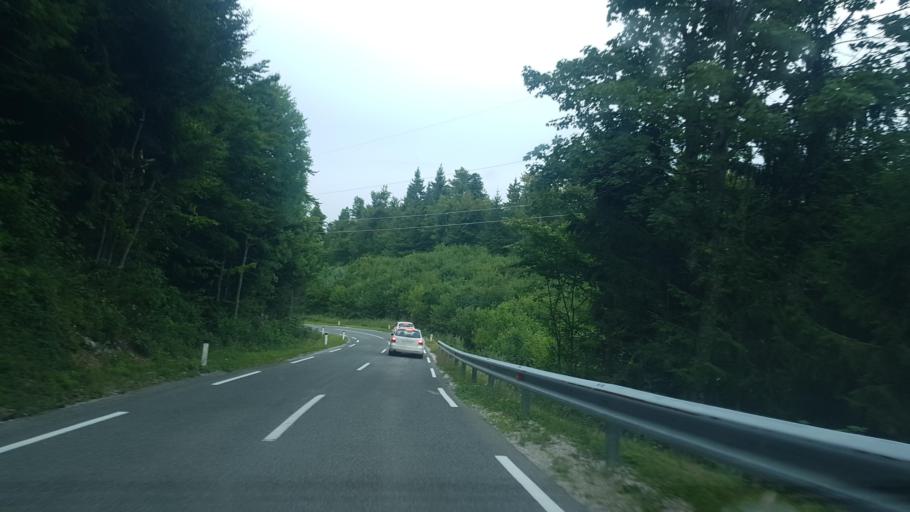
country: SI
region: Logatec
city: Logatec
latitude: 45.8783
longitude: 14.1556
